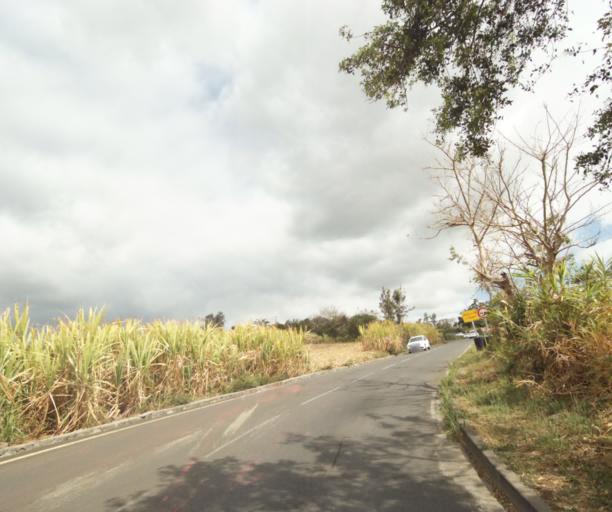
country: RE
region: Reunion
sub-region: Reunion
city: Saint-Paul
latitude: -21.0347
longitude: 55.2879
